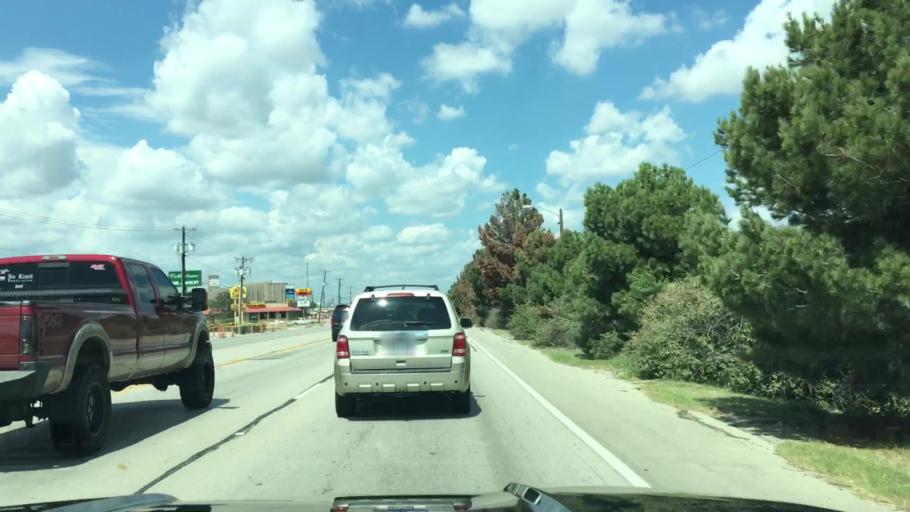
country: US
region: Texas
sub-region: Tarrant County
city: Saginaw
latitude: 32.8517
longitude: -97.3605
